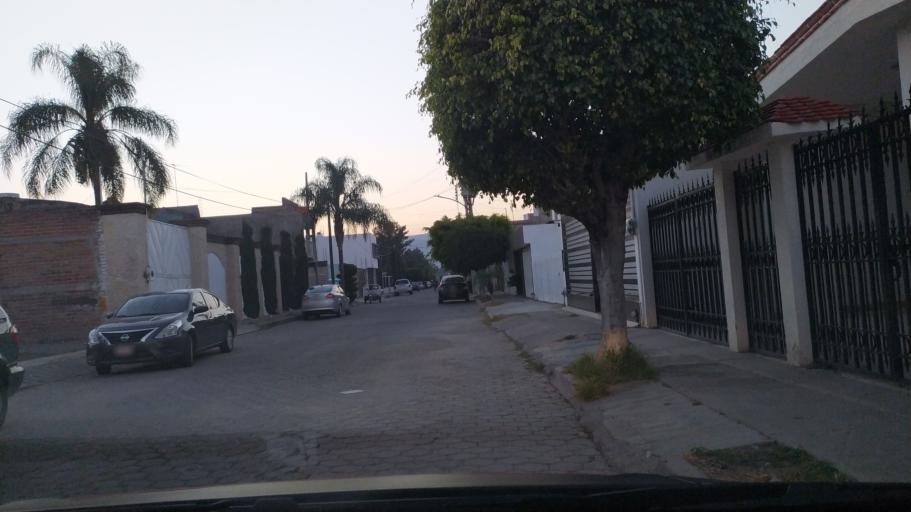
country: MX
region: Guanajuato
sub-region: Purisima del Rincon
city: Monte Grande
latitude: 21.0067
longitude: -101.8603
